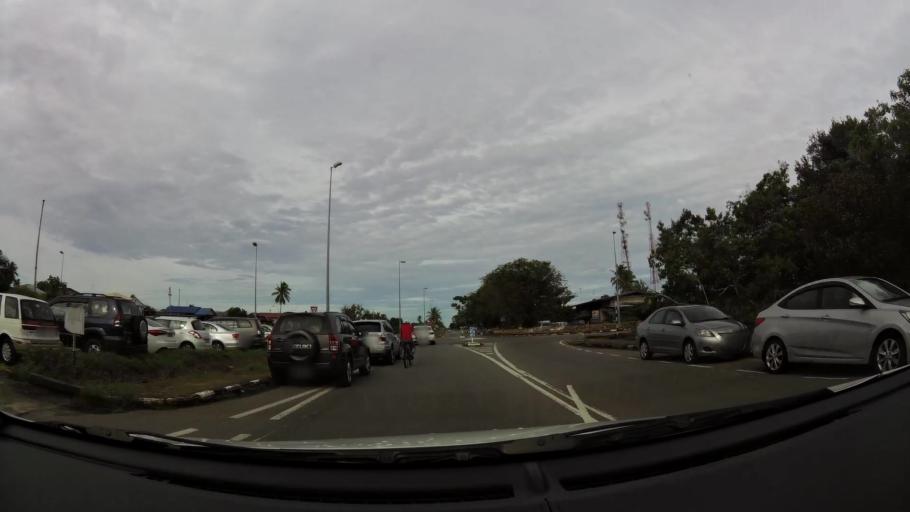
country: BN
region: Belait
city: Seria
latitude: 4.6134
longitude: 114.3351
